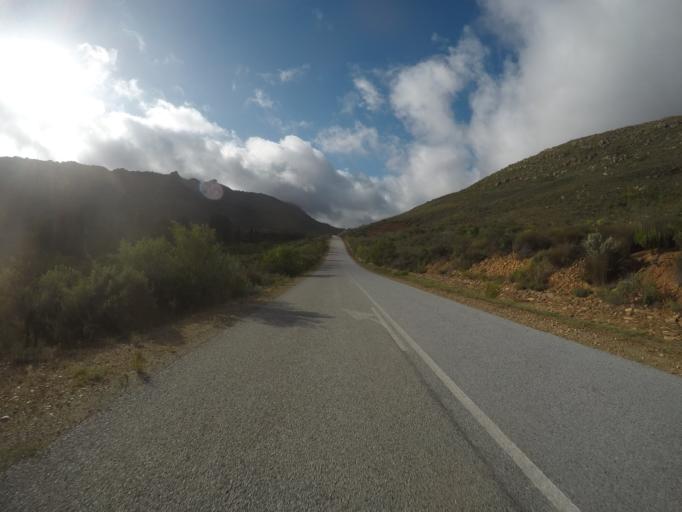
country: ZA
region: Western Cape
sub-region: West Coast District Municipality
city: Clanwilliam
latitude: -32.3649
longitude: 18.8589
